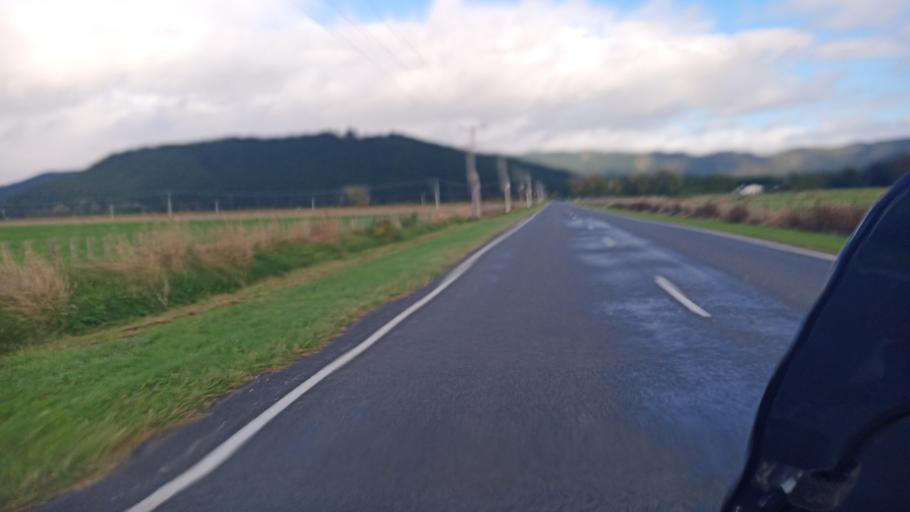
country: NZ
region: Gisborne
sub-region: Gisborne District
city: Gisborne
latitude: -38.6340
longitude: 177.8622
